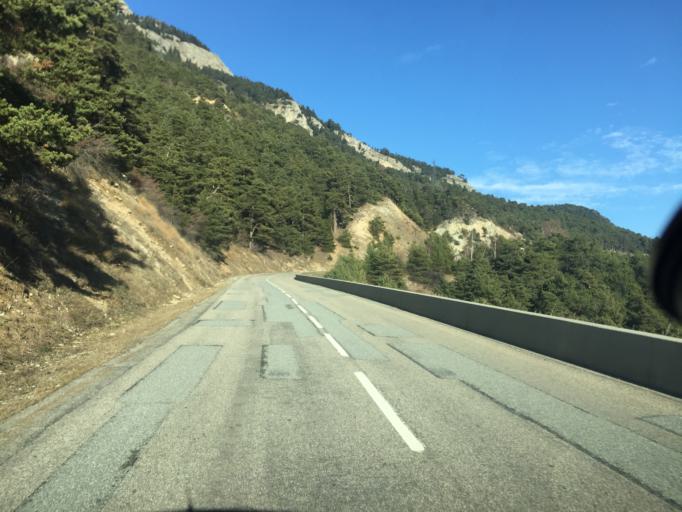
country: FR
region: Rhone-Alpes
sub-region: Departement de la Savoie
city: Modane
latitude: 45.2188
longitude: 6.7127
